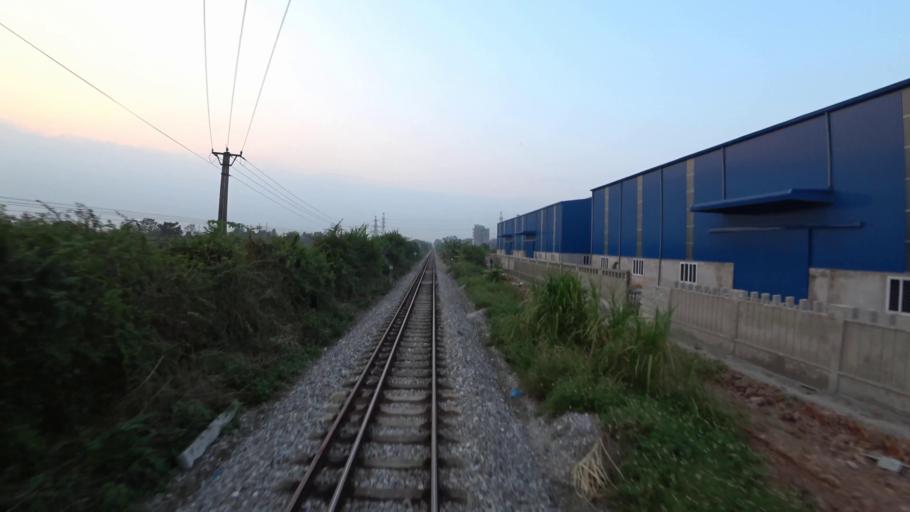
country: VN
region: Ha Noi
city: Dong Anh
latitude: 21.1463
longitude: 105.8600
